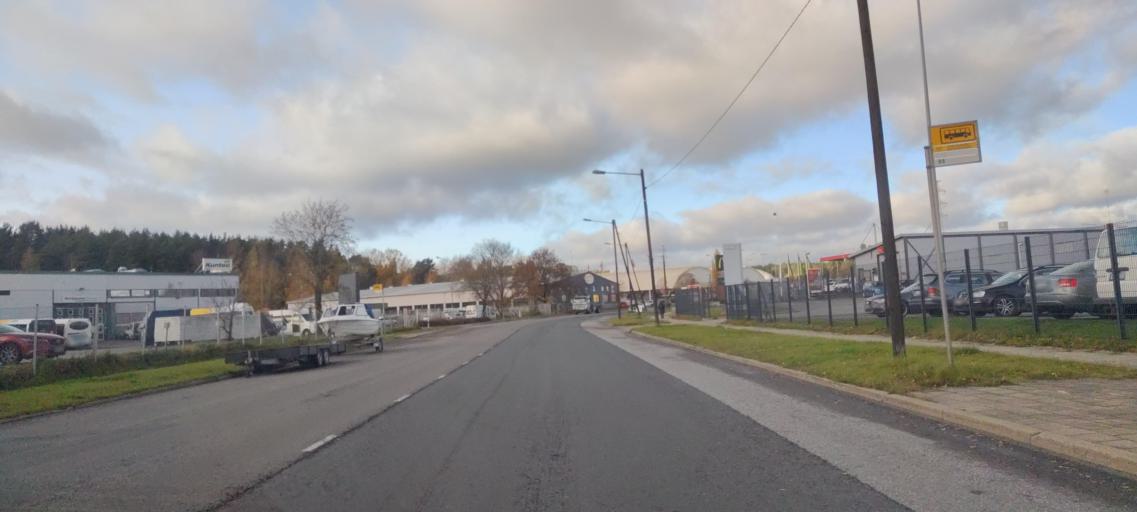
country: FI
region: Varsinais-Suomi
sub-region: Turku
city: Turku
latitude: 60.4751
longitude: 22.2576
